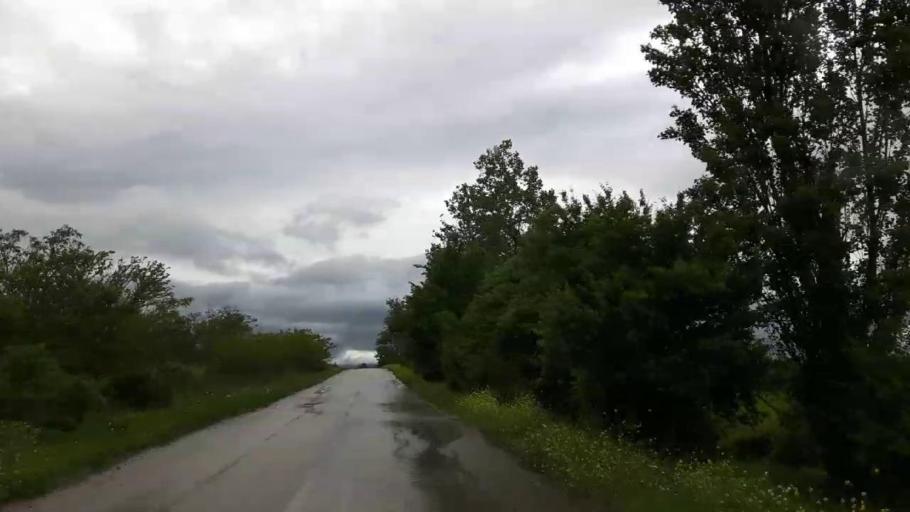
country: GE
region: Shida Kartli
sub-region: Khashuris Raioni
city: Khashuri
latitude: 41.9921
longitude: 43.7164
